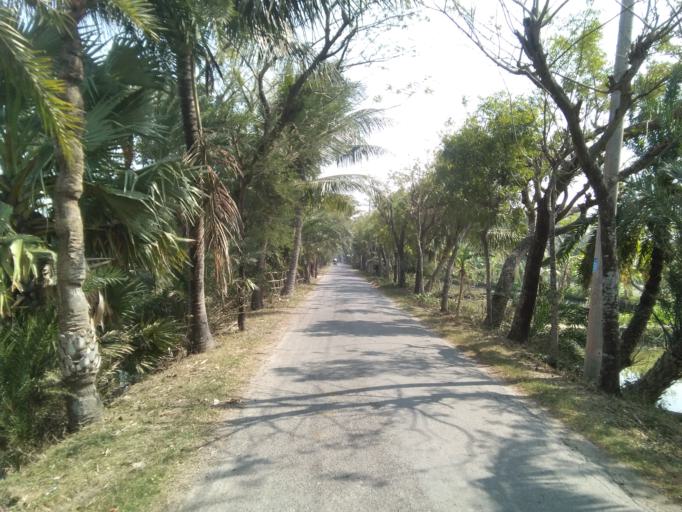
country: IN
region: West Bengal
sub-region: North 24 Parganas
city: Taki
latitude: 22.5927
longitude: 88.9897
